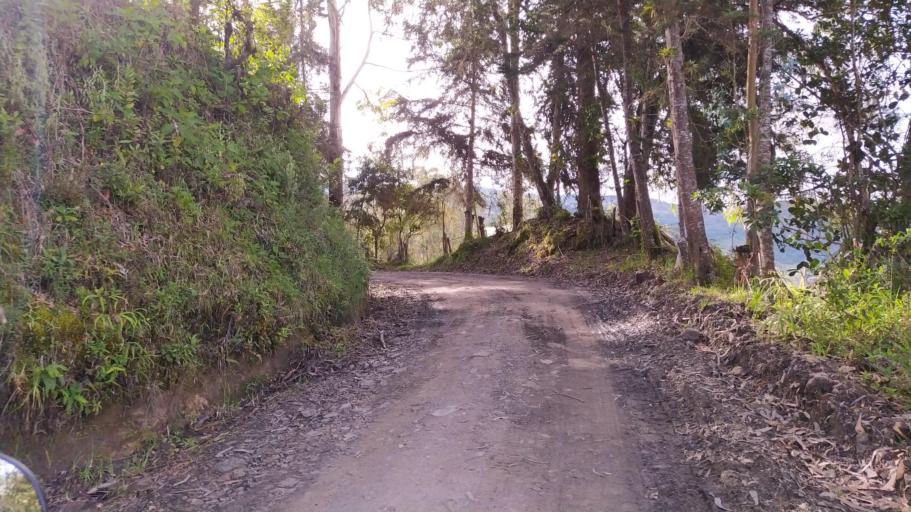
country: CO
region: Cundinamarca
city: Tenza
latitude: 5.0904
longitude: -73.4751
